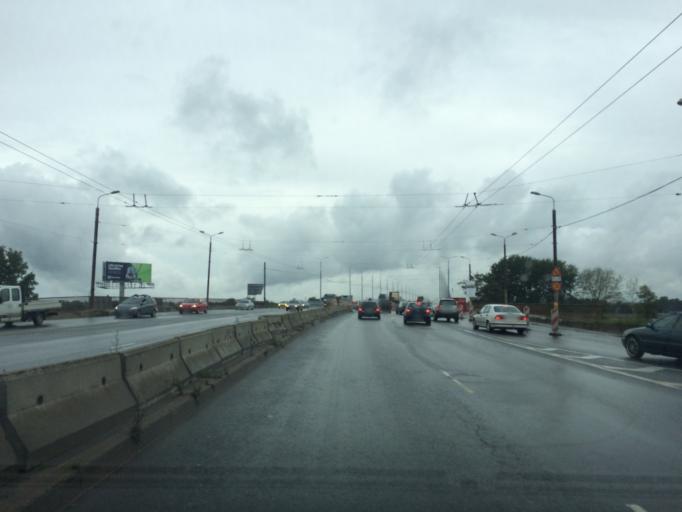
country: LV
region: Riga
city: Riga
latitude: 56.9384
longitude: 24.1286
